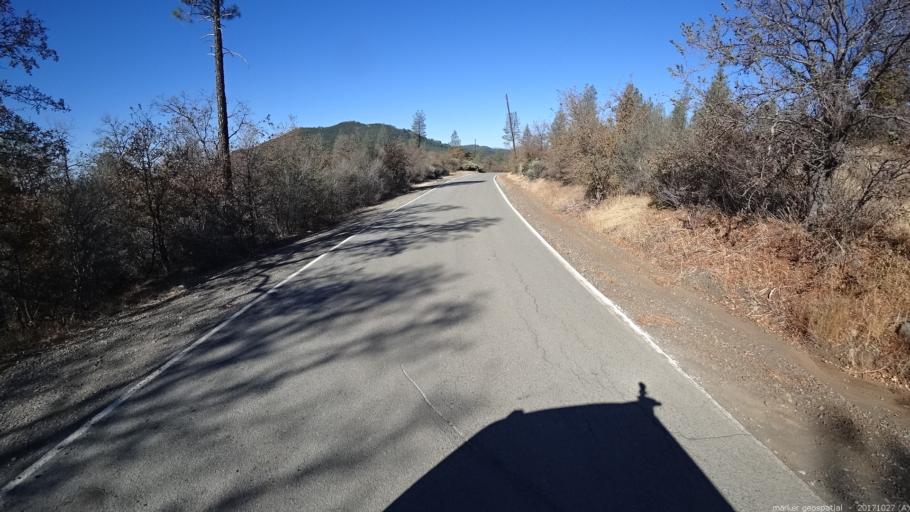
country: US
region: California
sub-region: Shasta County
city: Burney
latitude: 40.7975
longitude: -121.9243
